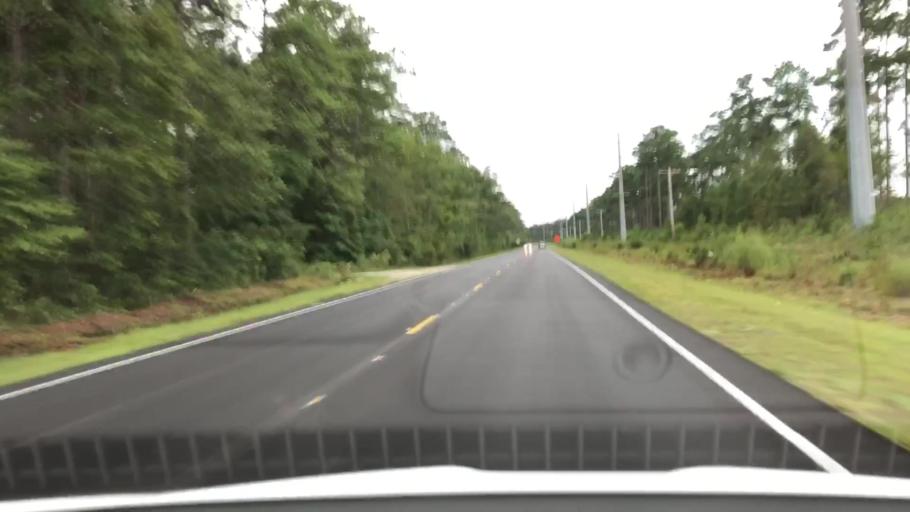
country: US
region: North Carolina
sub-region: Onslow County
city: Swansboro
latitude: 34.7813
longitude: -77.1099
